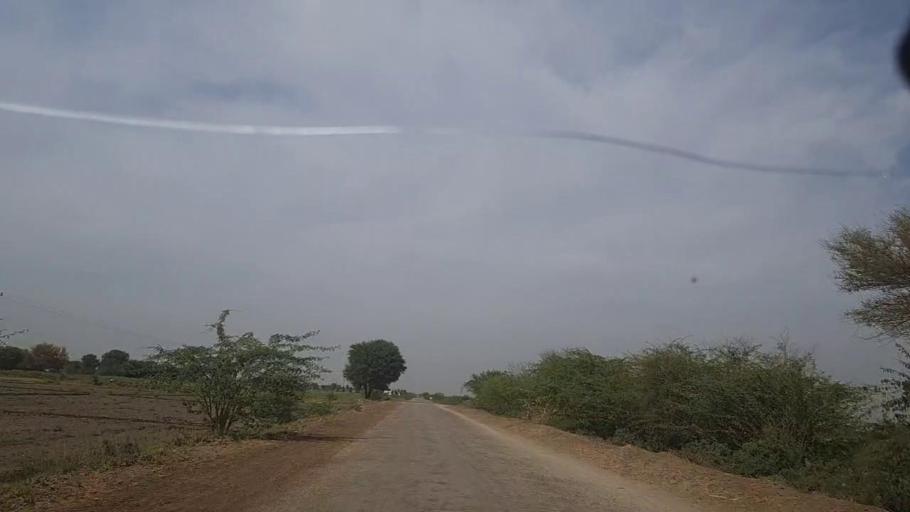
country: PK
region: Sindh
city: Pithoro
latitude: 25.5579
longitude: 69.3628
